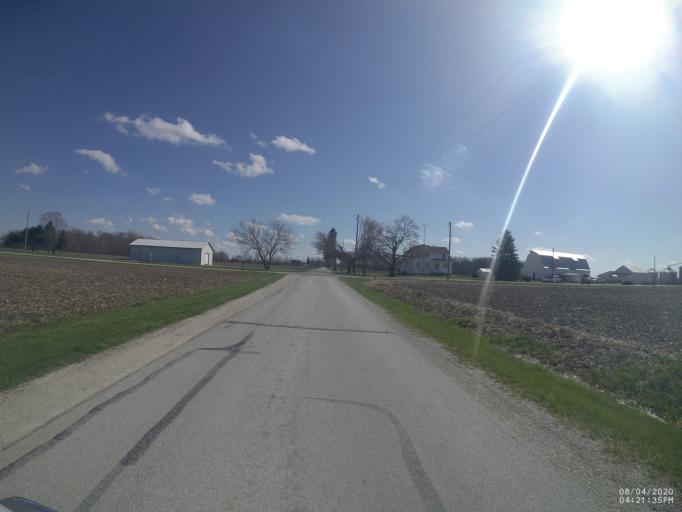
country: US
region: Ohio
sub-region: Sandusky County
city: Stony Prairie
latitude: 41.2829
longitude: -83.2165
